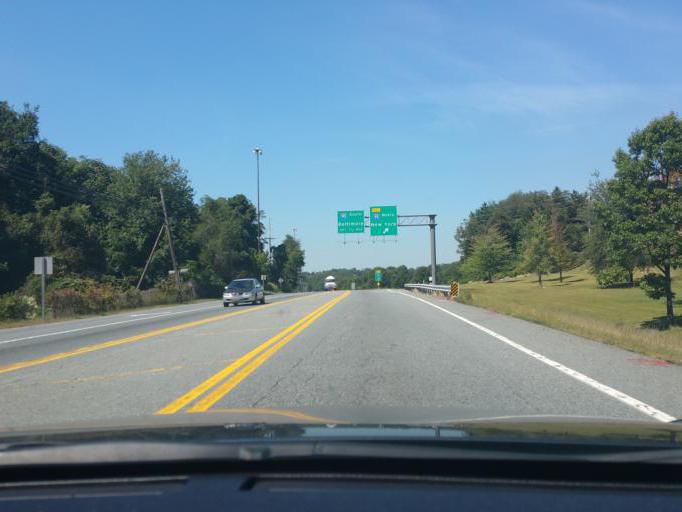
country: US
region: Maryland
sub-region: Harford County
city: Havre de Grace
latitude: 39.5683
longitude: -76.1312
